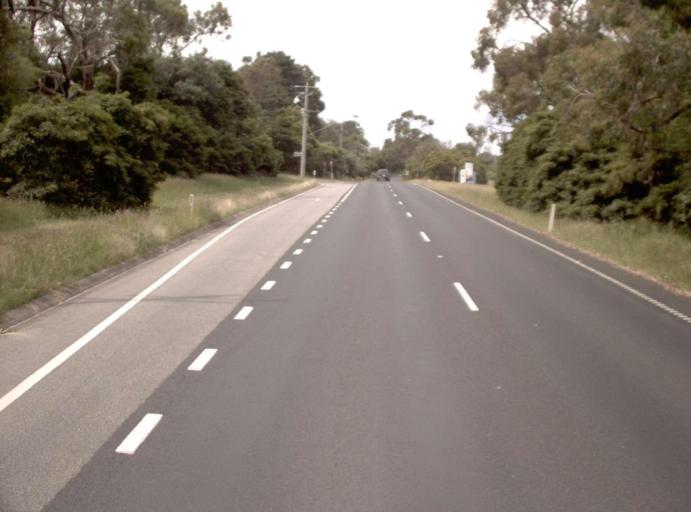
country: AU
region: Victoria
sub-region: Mornington Peninsula
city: Baxter
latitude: -38.1947
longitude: 145.1344
